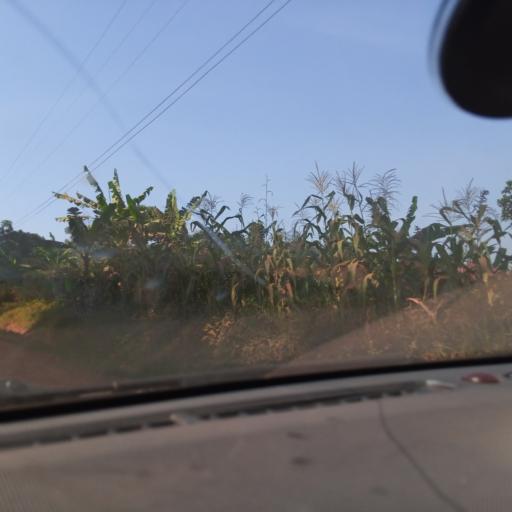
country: UG
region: Central Region
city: Masaka
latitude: -0.3301
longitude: 31.7331
